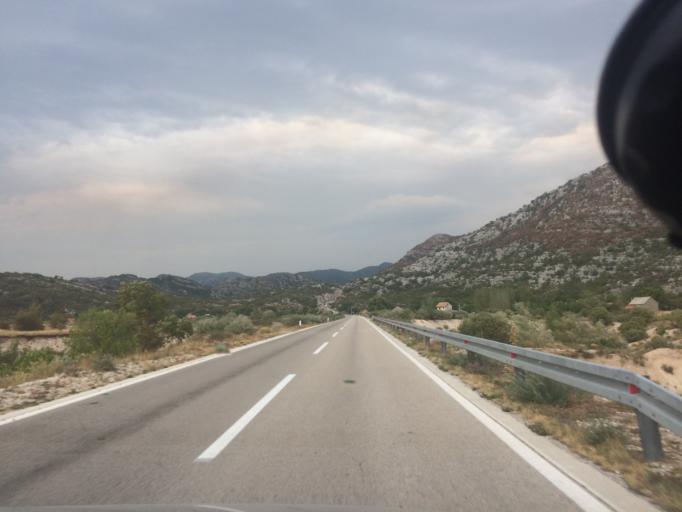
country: ME
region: Kotor
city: Risan
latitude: 42.6170
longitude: 18.6818
